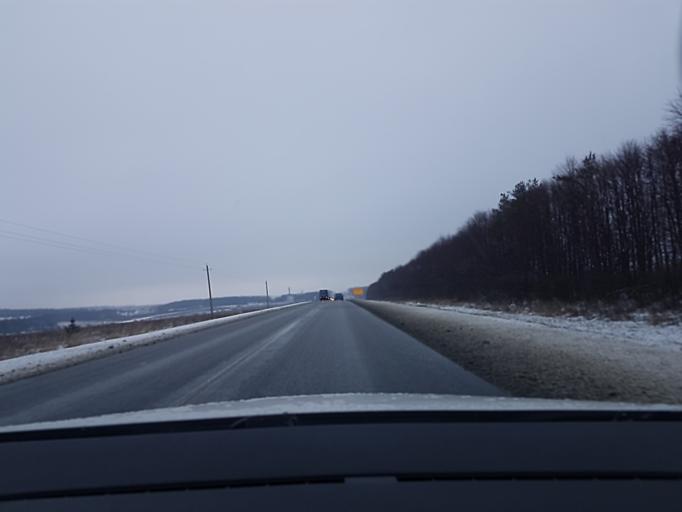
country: RU
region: Moskovskaya
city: Ozherel'ye
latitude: 54.7394
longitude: 38.2479
